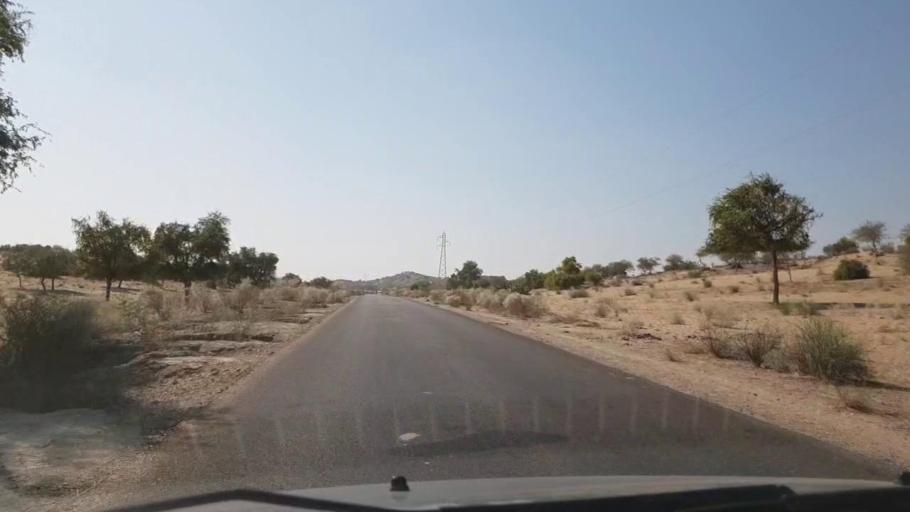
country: PK
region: Sindh
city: Mithi
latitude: 24.6853
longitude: 69.7845
